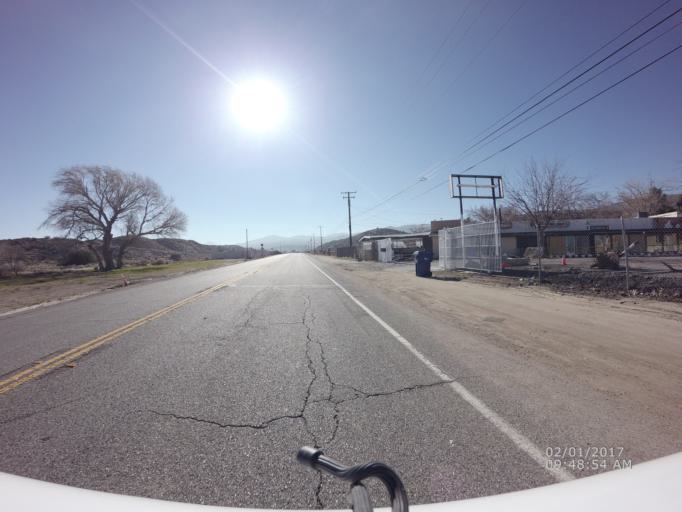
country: US
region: California
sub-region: Los Angeles County
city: Vincent
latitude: 34.5386
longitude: -118.1059
